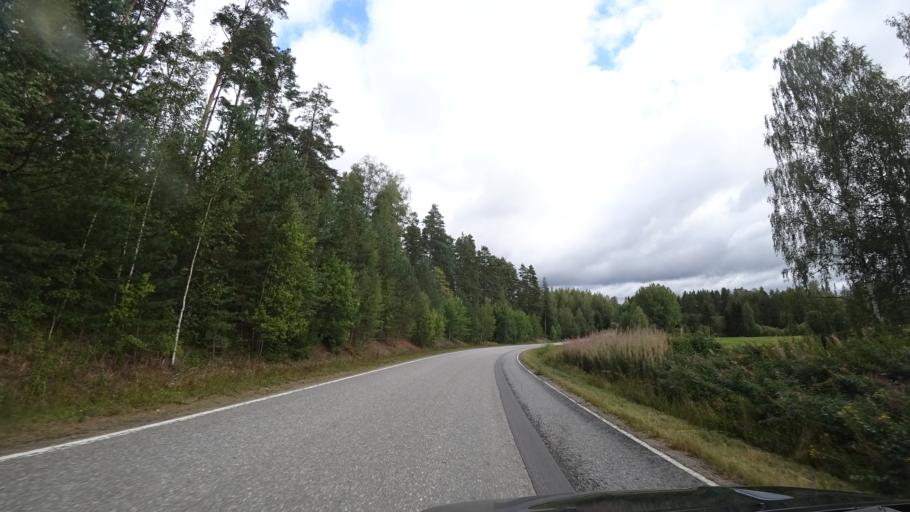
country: FI
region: Haeme
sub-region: Haemeenlinna
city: Lammi
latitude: 60.9861
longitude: 25.0183
